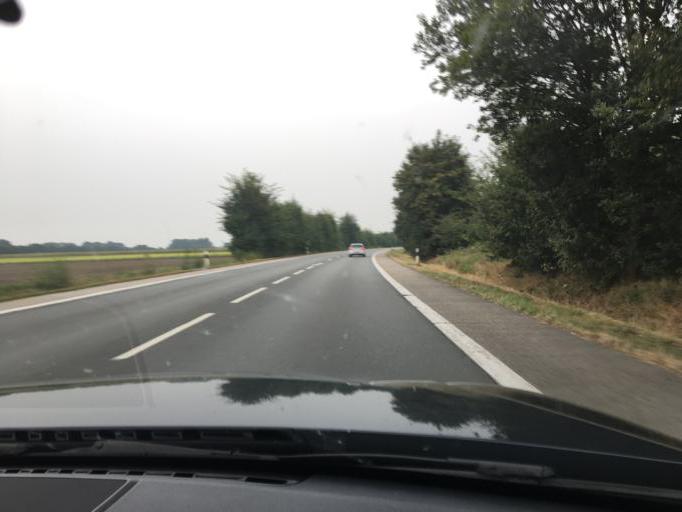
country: DE
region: North Rhine-Westphalia
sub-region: Regierungsbezirk Munster
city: Greven
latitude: 52.0775
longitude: 7.6568
